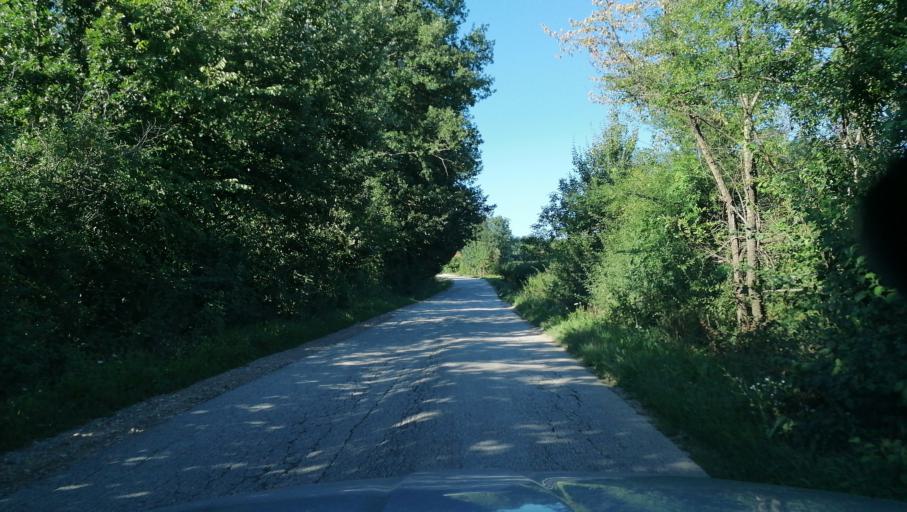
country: RS
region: Central Serbia
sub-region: Sumadijski Okrug
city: Knic
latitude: 43.8841
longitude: 20.6146
